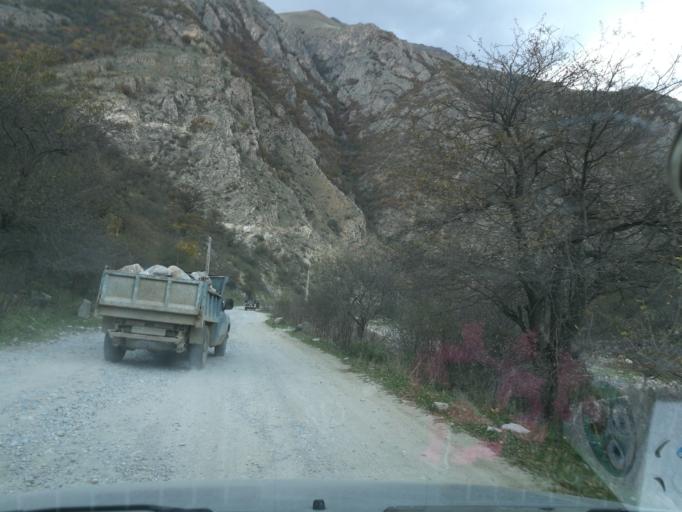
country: IR
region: Mazandaran
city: `Abbasabad
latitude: 36.4443
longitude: 51.0635
